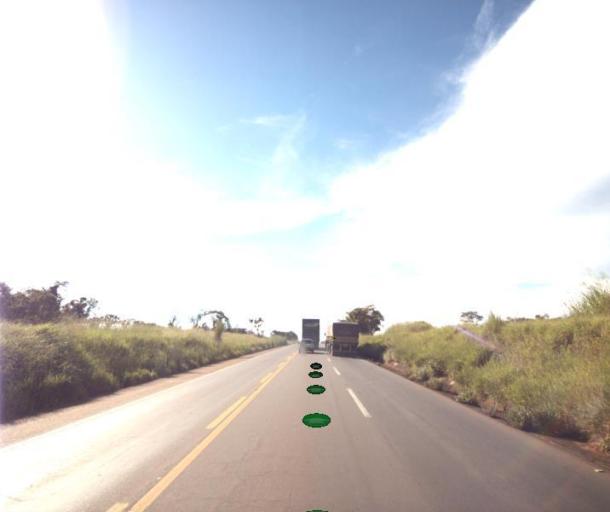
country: BR
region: Goias
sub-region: Rialma
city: Rialma
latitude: -15.3821
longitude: -49.5532
